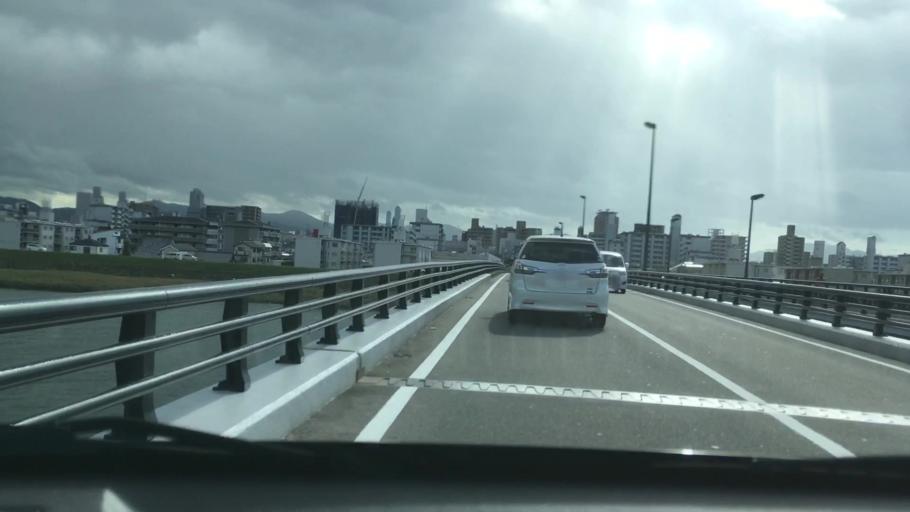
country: JP
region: Hiroshima
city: Hiroshima-shi
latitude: 34.3991
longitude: 132.4321
